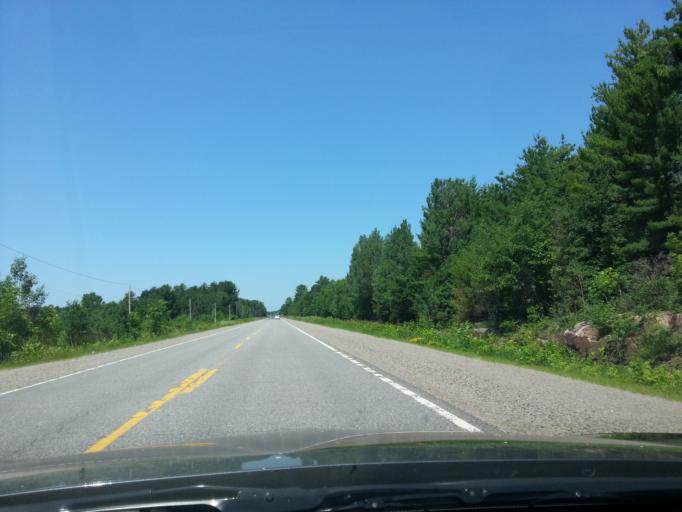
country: CA
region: Ontario
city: Arnprior
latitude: 45.5298
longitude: -76.3066
